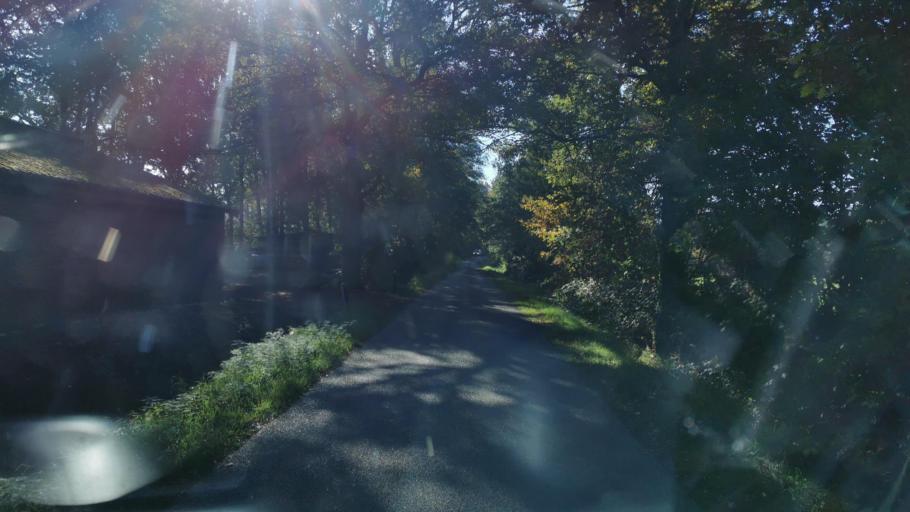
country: NL
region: Overijssel
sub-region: Gemeente Enschede
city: Enschede
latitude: 52.2576
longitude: 6.9160
